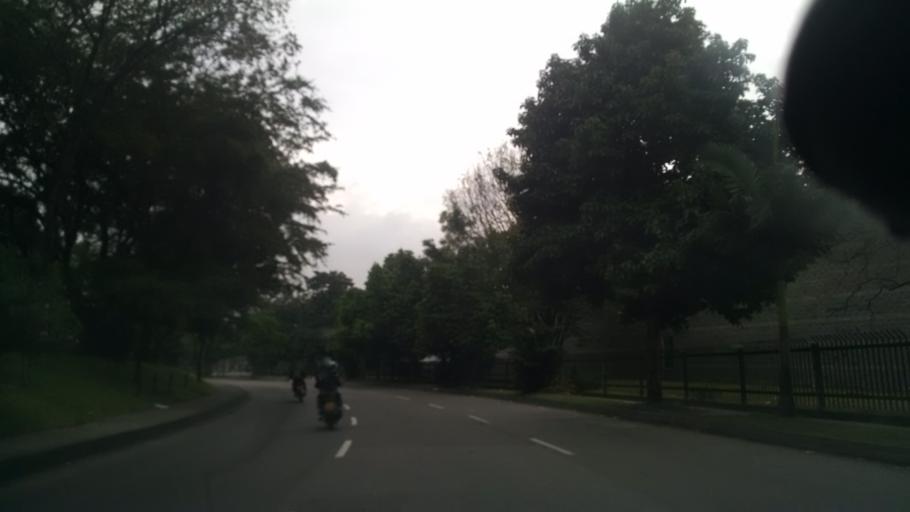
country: CO
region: Antioquia
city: Medellin
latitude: 6.2527
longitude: -75.5859
